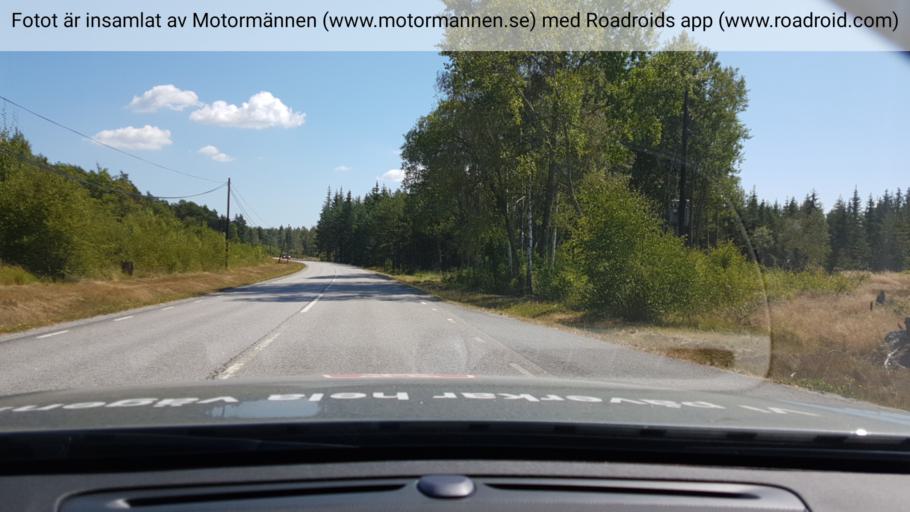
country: SE
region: Stockholm
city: Stenhamra
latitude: 59.3755
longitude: 17.6961
